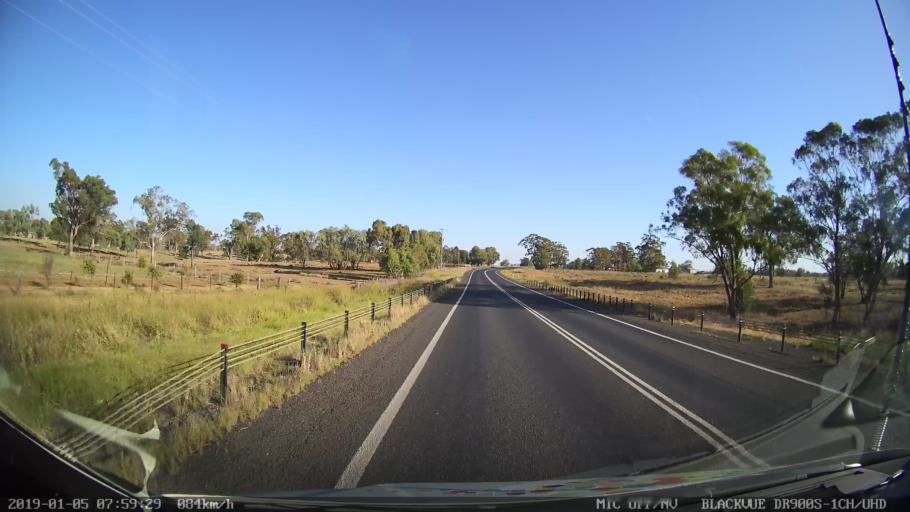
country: AU
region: New South Wales
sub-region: Gilgandra
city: Gilgandra
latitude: -31.7016
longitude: 148.6792
